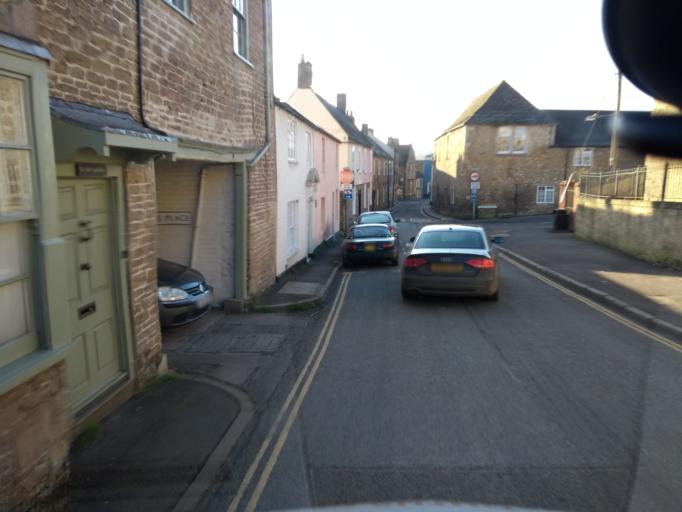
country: GB
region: England
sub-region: Somerset
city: Bruton
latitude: 51.1134
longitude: -2.4536
